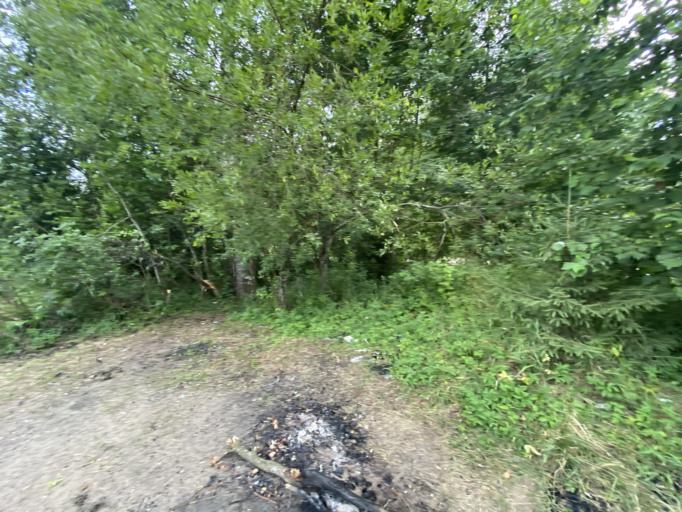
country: RU
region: Leningrad
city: Nurma
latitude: 59.5810
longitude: 31.1881
